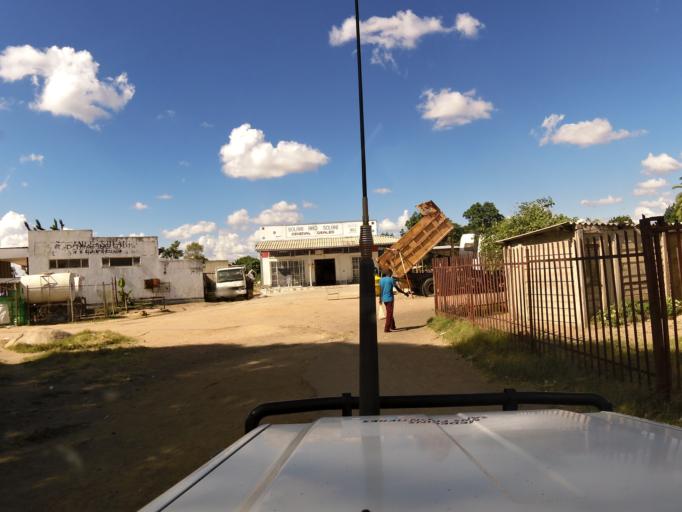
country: ZW
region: Harare
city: Epworth
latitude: -17.8767
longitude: 31.1262
